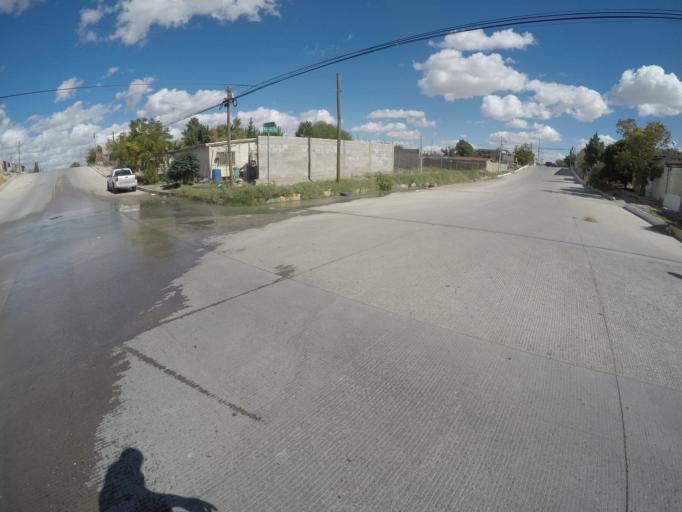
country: MX
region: Chihuahua
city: Ciudad Juarez
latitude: 31.6919
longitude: -106.4833
